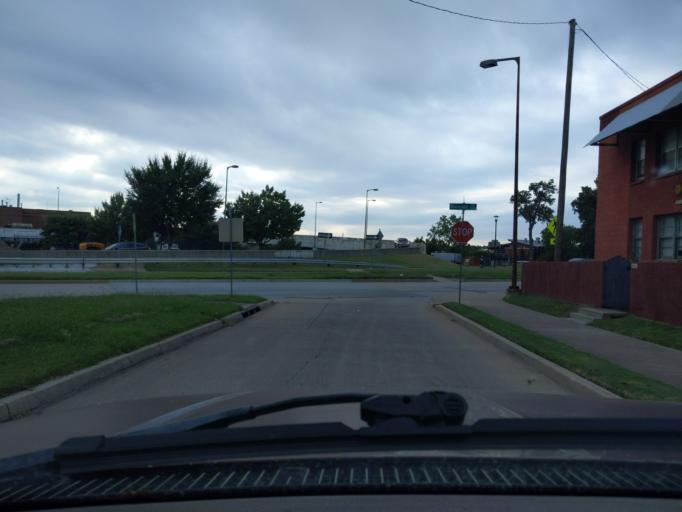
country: US
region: Oklahoma
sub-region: Tulsa County
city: Tulsa
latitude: 36.1334
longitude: -95.9903
